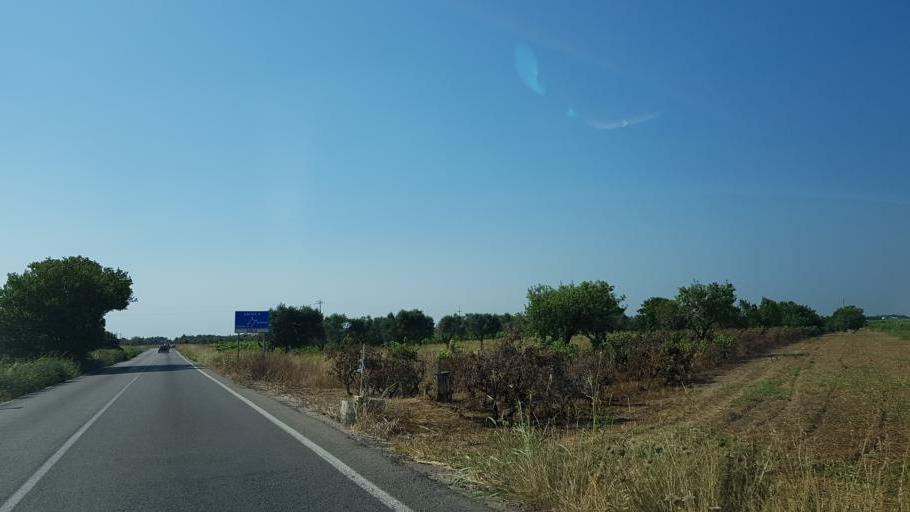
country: IT
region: Apulia
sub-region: Provincia di Lecce
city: Guagnano
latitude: 40.4240
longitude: 17.9475
